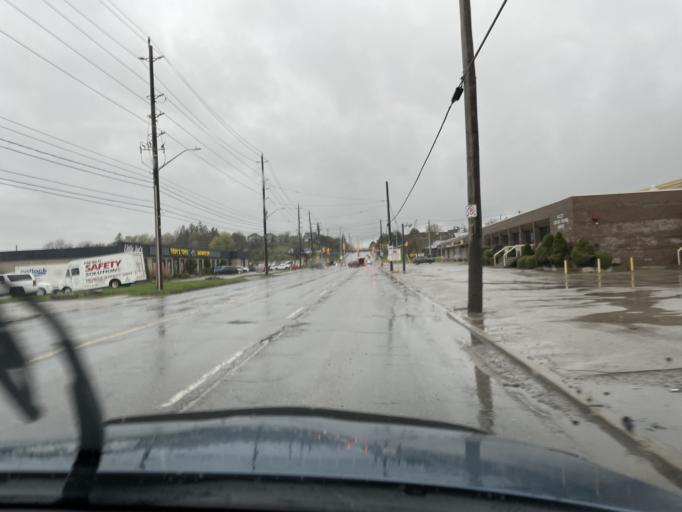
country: CA
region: Ontario
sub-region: Wellington County
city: Guelph
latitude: 43.5543
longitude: -80.2272
